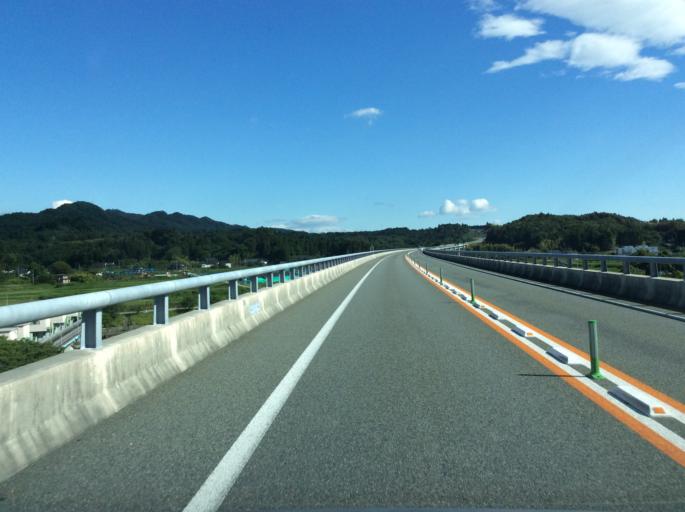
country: JP
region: Fukushima
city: Namie
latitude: 37.2760
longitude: 140.9823
